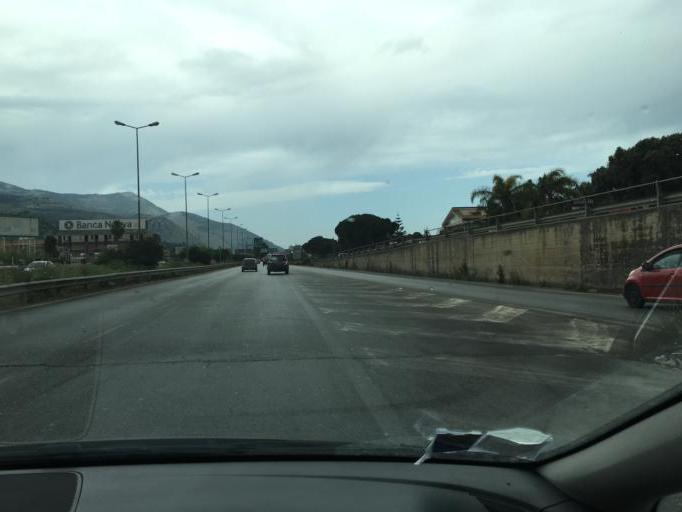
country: IT
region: Sicily
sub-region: Palermo
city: Palermo
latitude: 38.1500
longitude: 13.3250
